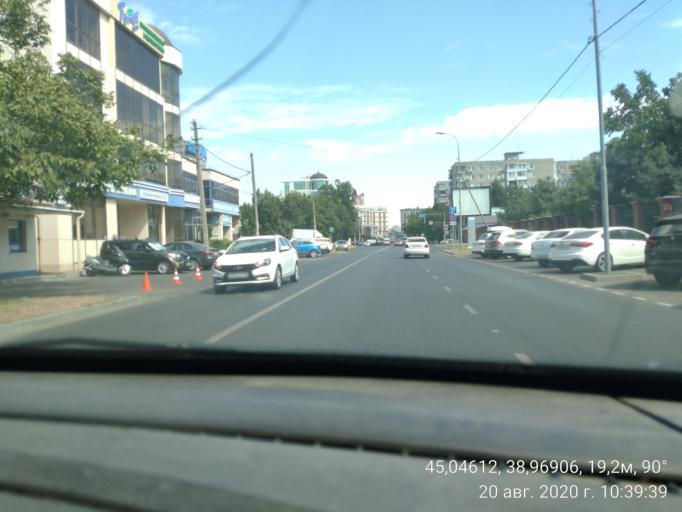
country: RU
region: Krasnodarskiy
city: Krasnodar
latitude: 45.0462
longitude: 38.9691
